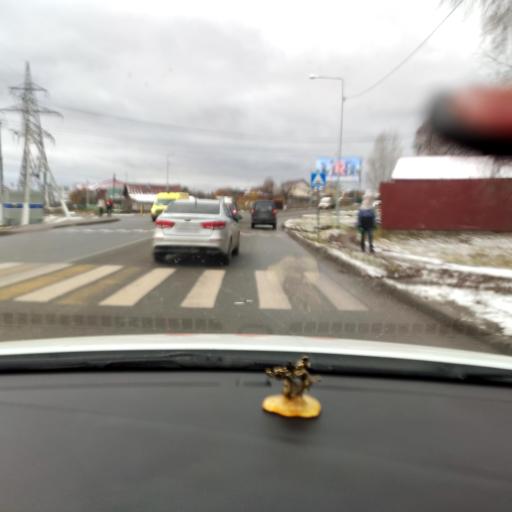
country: RU
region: Tatarstan
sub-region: Zelenodol'skiy Rayon
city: Zelenodolsk
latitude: 55.8474
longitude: 48.5395
